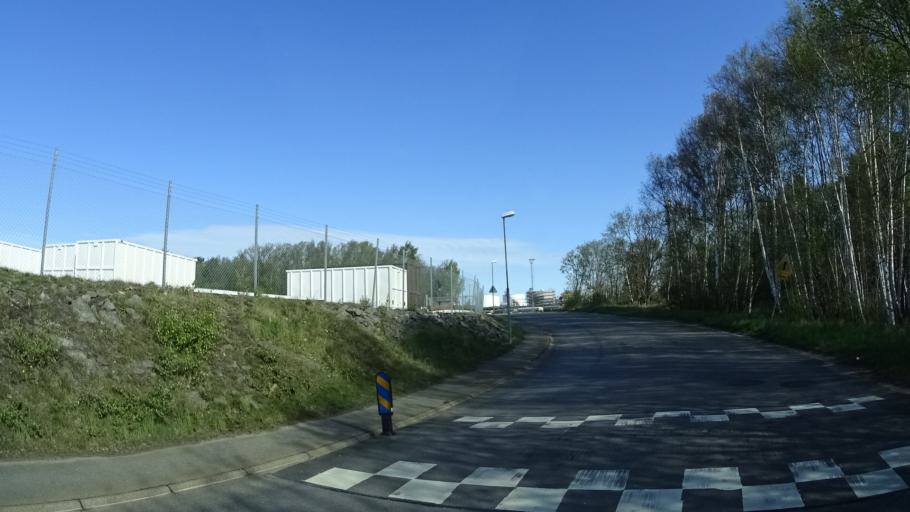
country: SE
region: Vaestra Goetaland
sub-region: Stenungsunds Kommun
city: Stenungsund
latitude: 58.0802
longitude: 11.8232
